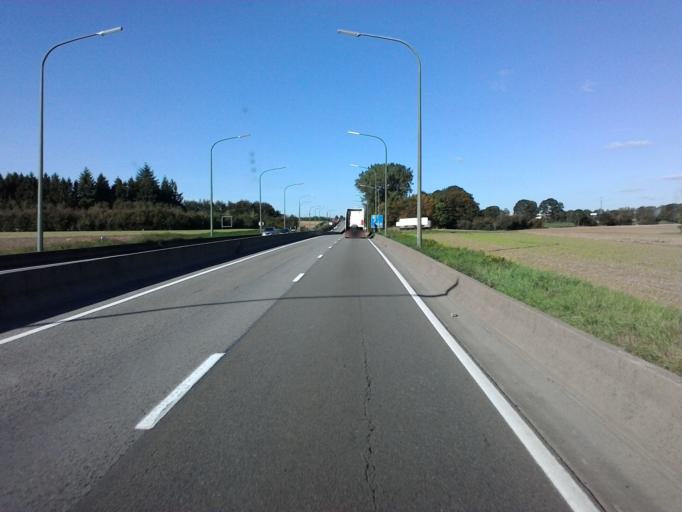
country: BE
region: Wallonia
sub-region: Province du Luxembourg
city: Arlon
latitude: 49.6423
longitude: 5.8164
